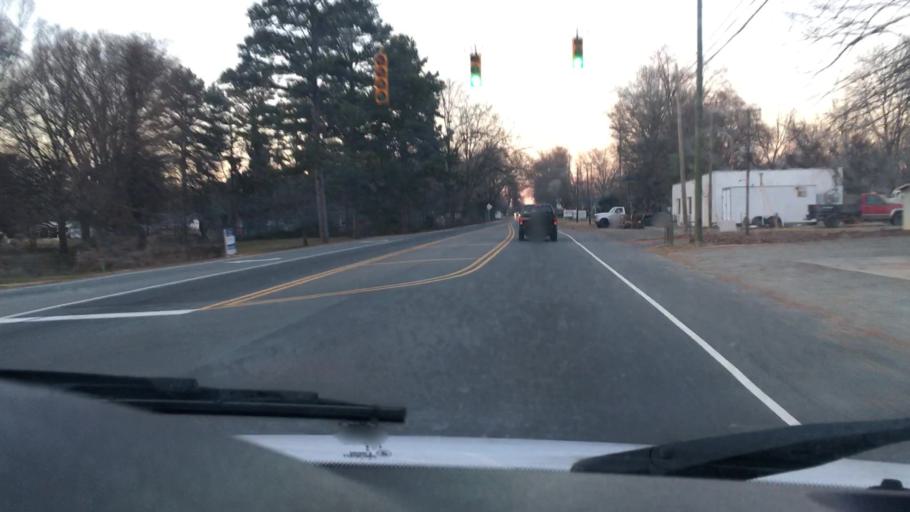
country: US
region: North Carolina
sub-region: Mecklenburg County
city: Huntersville
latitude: 35.4265
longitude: -80.8427
